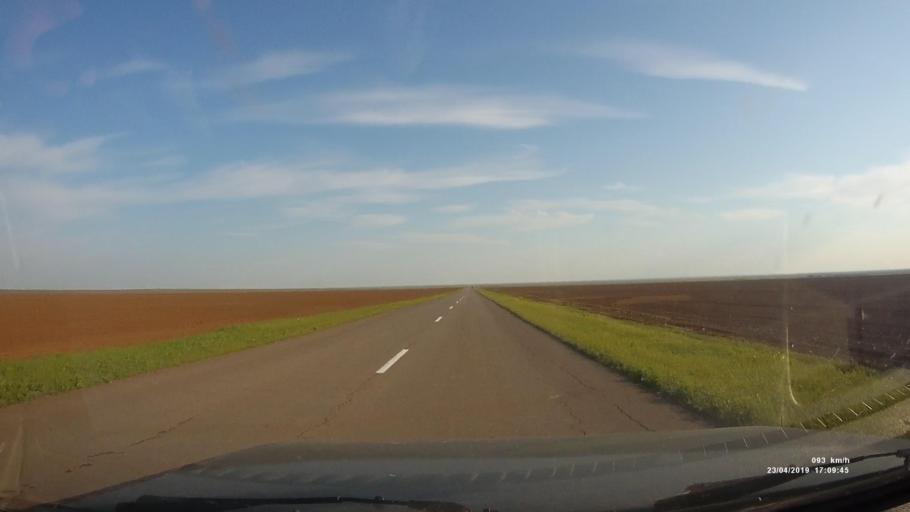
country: RU
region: Kalmykiya
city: Priyutnoye
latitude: 46.2541
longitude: 43.4842
